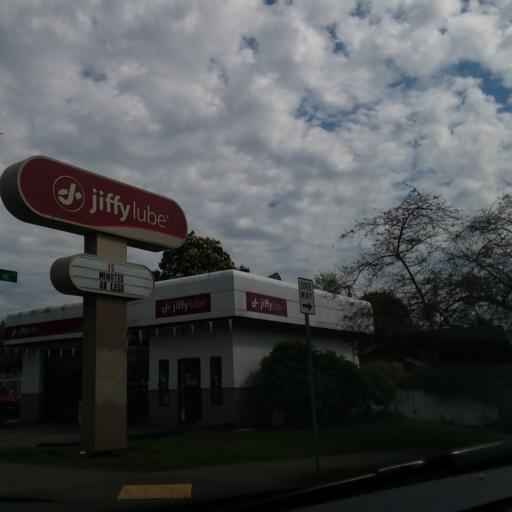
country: US
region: Washington
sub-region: King County
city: Seattle
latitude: 47.6613
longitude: -122.3262
